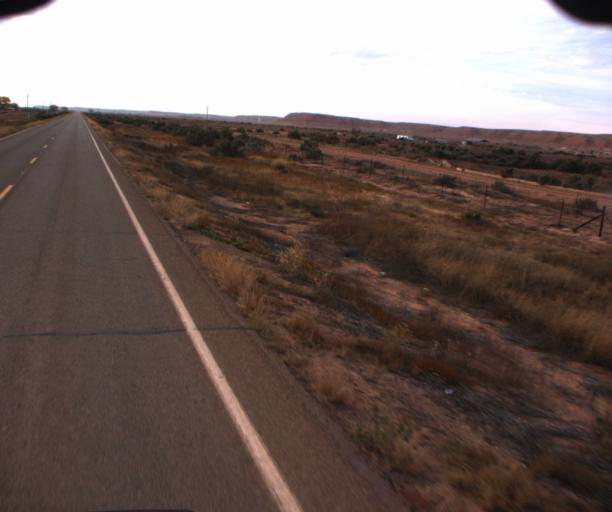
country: US
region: Arizona
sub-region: Apache County
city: Many Farms
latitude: 36.4157
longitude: -109.6070
